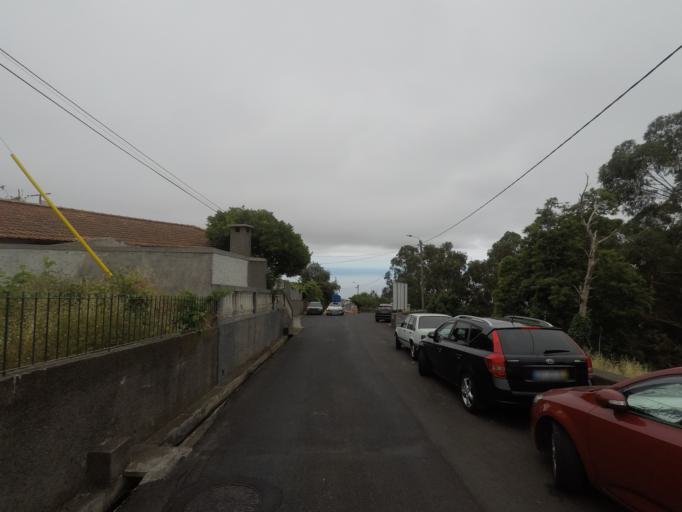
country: PT
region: Madeira
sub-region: Camara de Lobos
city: Curral das Freiras
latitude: 32.6813
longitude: -16.9495
